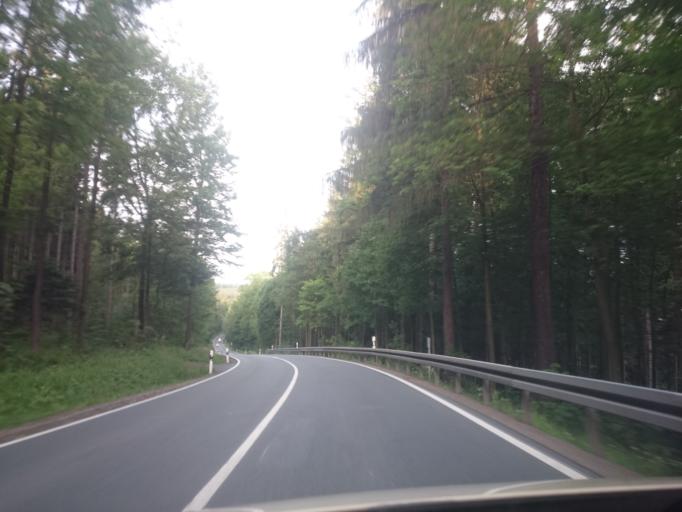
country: DE
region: Saxony
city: Lengefeld
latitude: 50.6997
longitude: 13.1559
